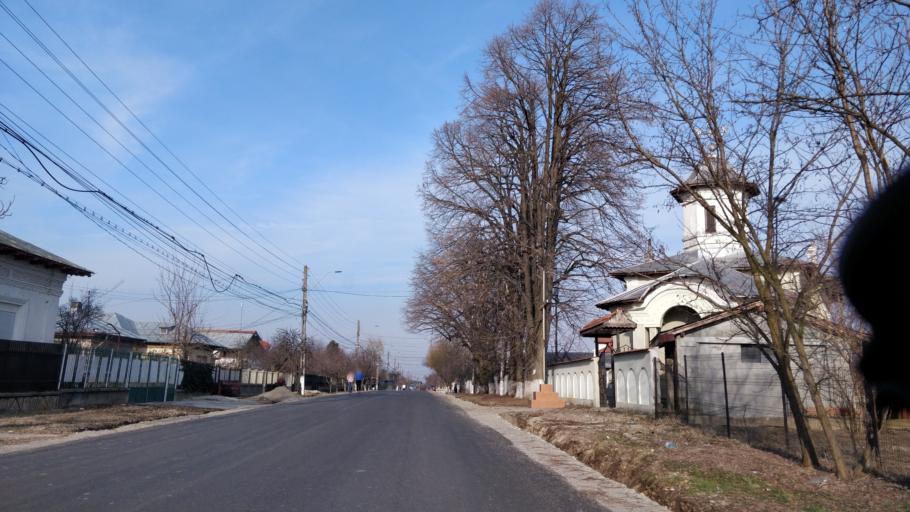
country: RO
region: Giurgiu
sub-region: Comuna Ulmi
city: Trestieni
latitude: 44.5057
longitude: 25.7598
